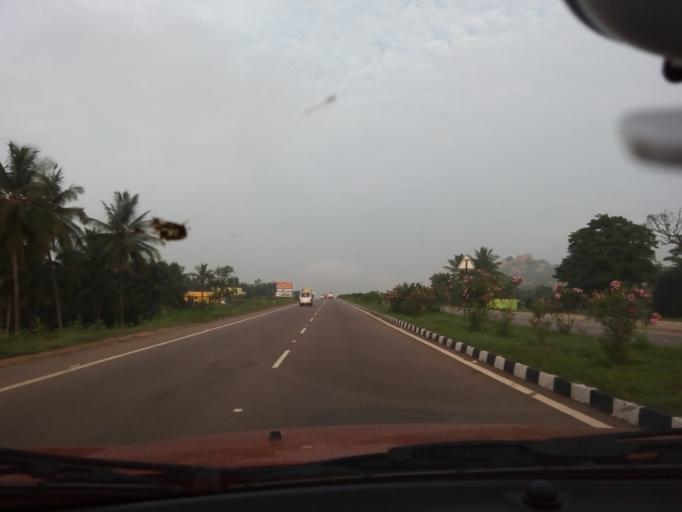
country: IN
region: Karnataka
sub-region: Ramanagara
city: Magadi
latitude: 13.0748
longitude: 77.1965
